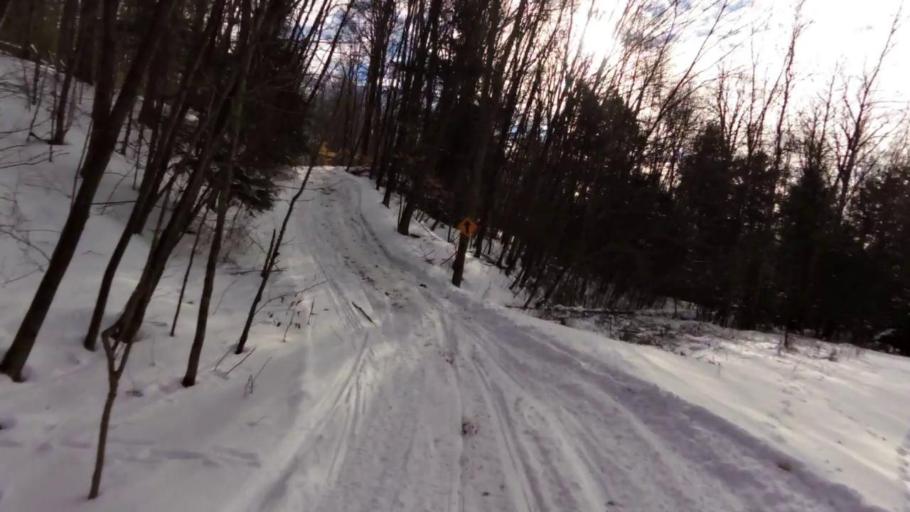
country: US
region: Pennsylvania
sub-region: McKean County
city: Foster Brook
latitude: 42.0084
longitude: -78.5947
